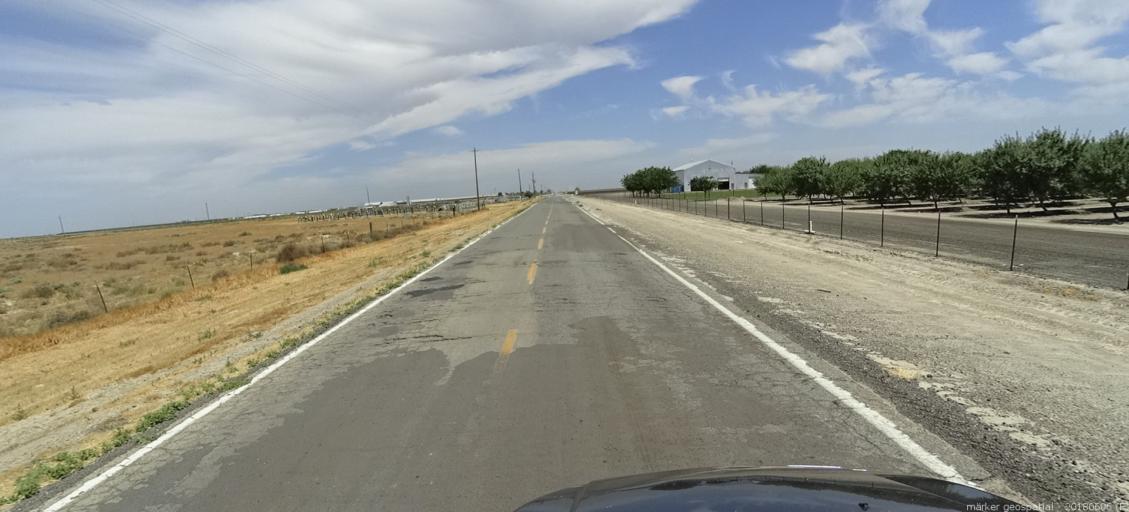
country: US
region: California
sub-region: Fresno County
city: Firebaugh
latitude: 36.9205
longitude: -120.3821
